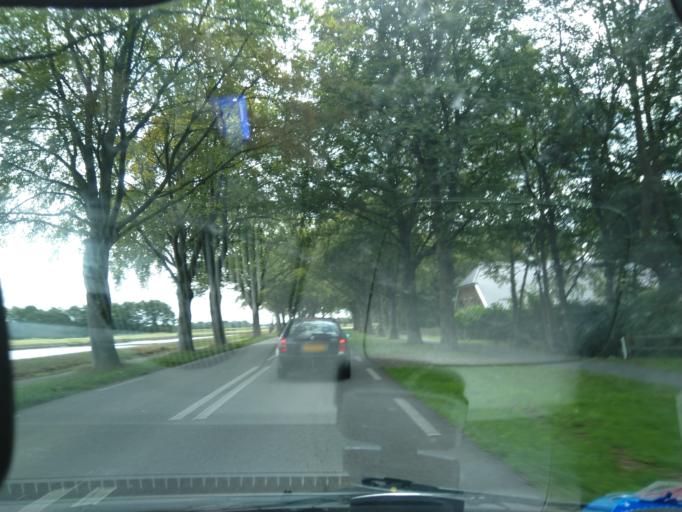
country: NL
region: Drenthe
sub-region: Gemeente Tynaarlo
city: Tynaarlo
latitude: 53.1067
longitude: 6.6045
